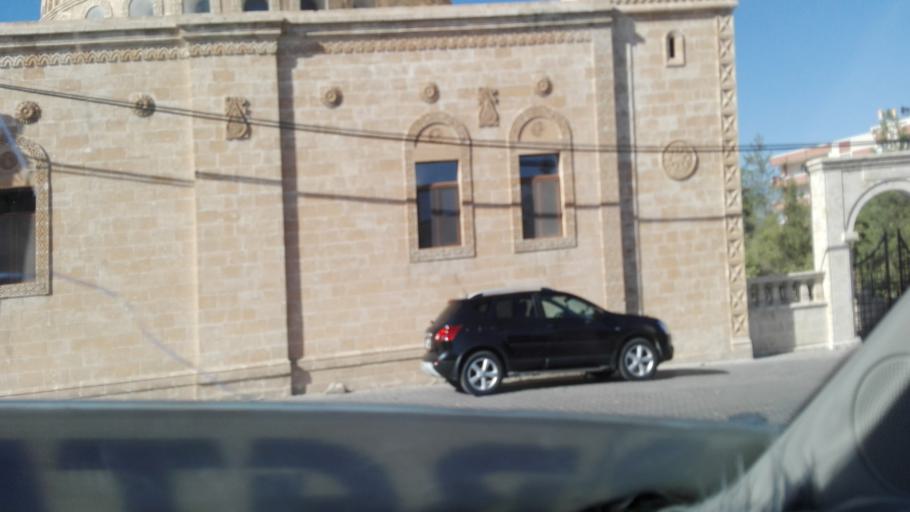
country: TR
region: Mardin
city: Midyat
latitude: 37.4277
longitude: 41.3383
